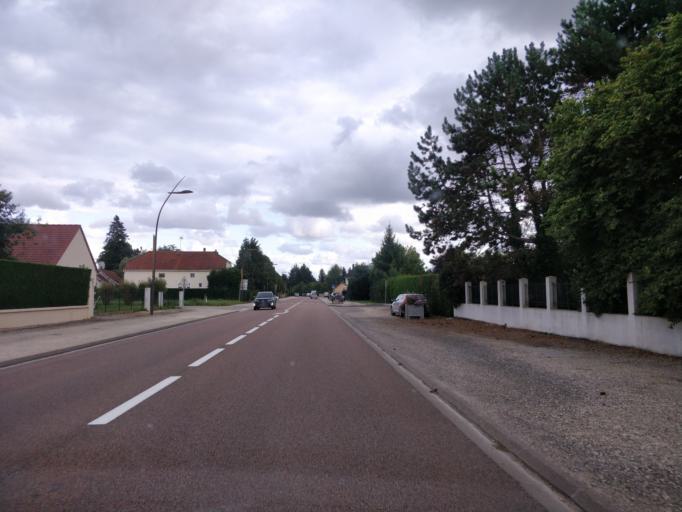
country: FR
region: Champagne-Ardenne
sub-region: Departement de l'Aube
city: Lusigny-sur-Barse
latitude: 48.2503
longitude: 4.2649
